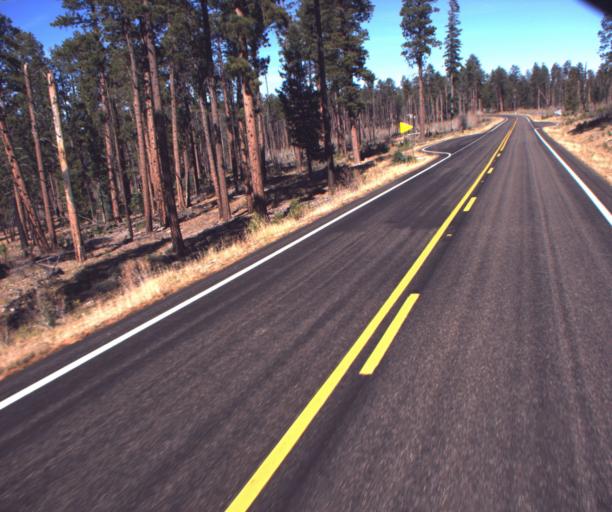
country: US
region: Arizona
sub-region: Coconino County
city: Fredonia
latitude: 36.6332
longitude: -112.1727
